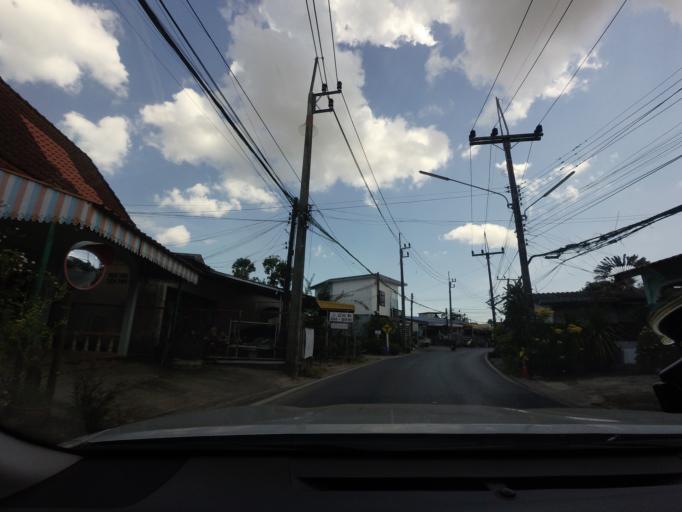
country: TH
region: Phuket
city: Thalang
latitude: 8.0169
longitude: 98.3177
